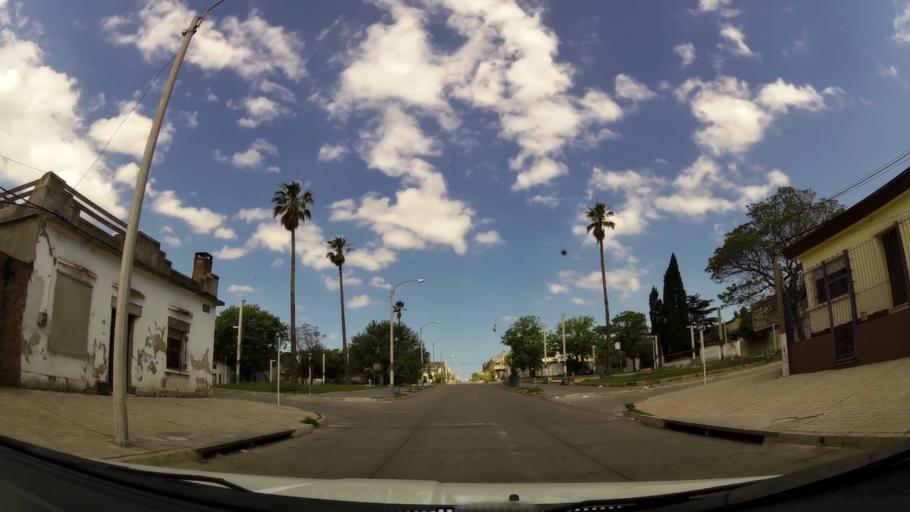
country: UY
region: Montevideo
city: Montevideo
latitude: -34.8489
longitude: -56.2327
